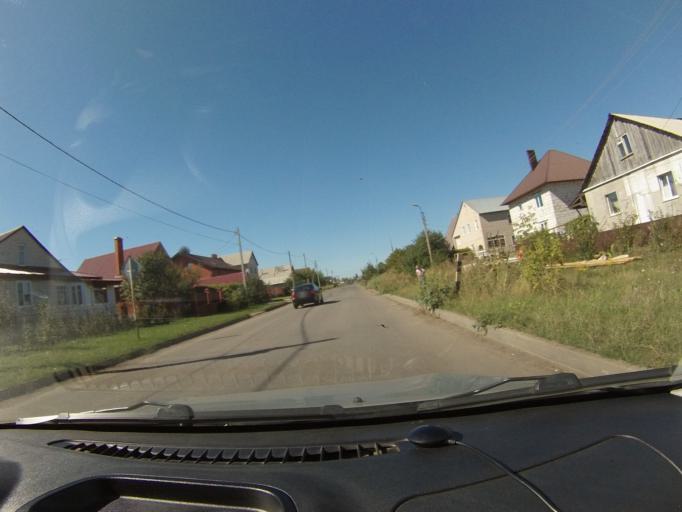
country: RU
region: Tambov
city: Tambov
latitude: 52.7618
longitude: 41.3729
